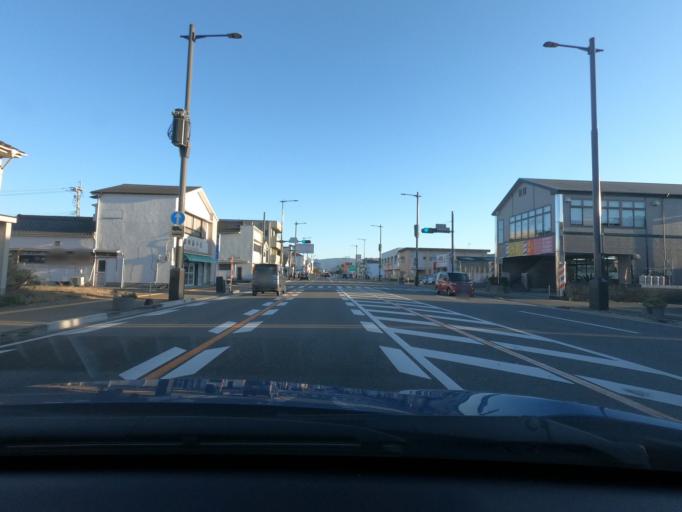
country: JP
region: Kagoshima
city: Satsumasendai
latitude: 31.8273
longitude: 130.2986
